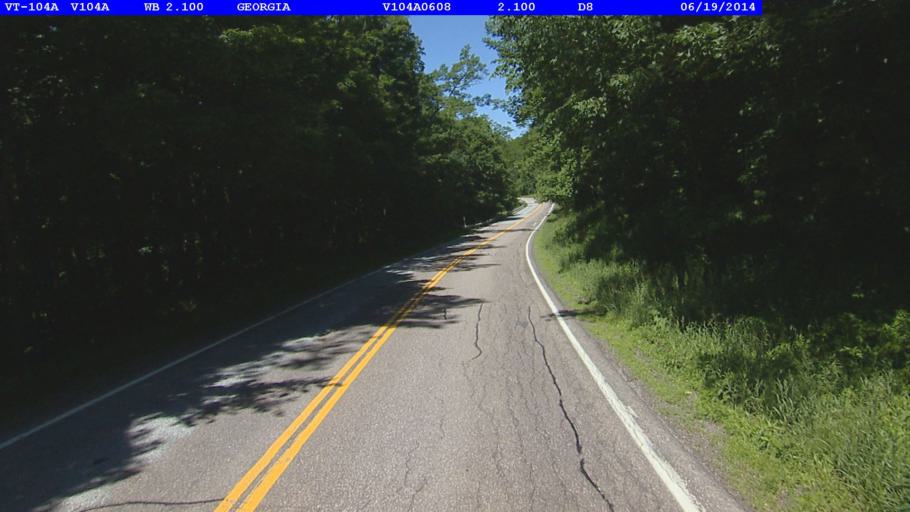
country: US
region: Vermont
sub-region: Chittenden County
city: Milton
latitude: 44.6799
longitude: -73.0748
